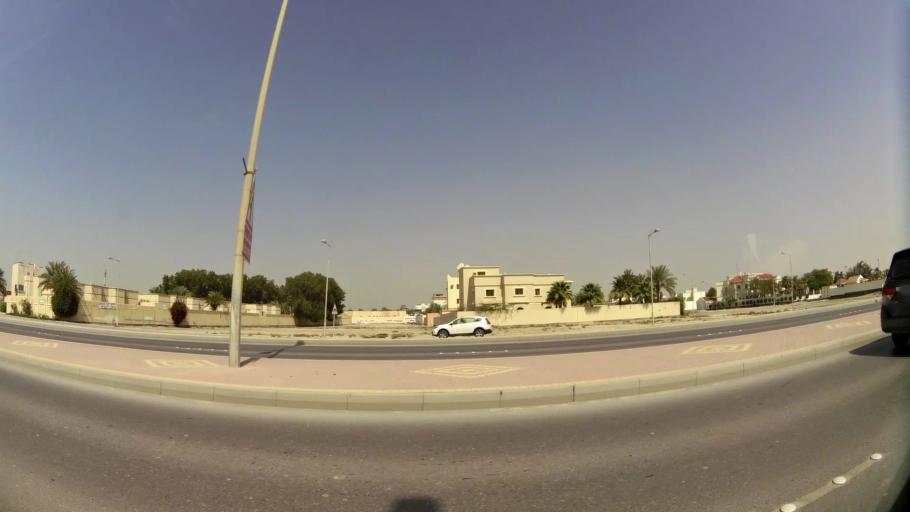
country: BH
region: Northern
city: Madinat `Isa
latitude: 26.1935
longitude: 50.4635
